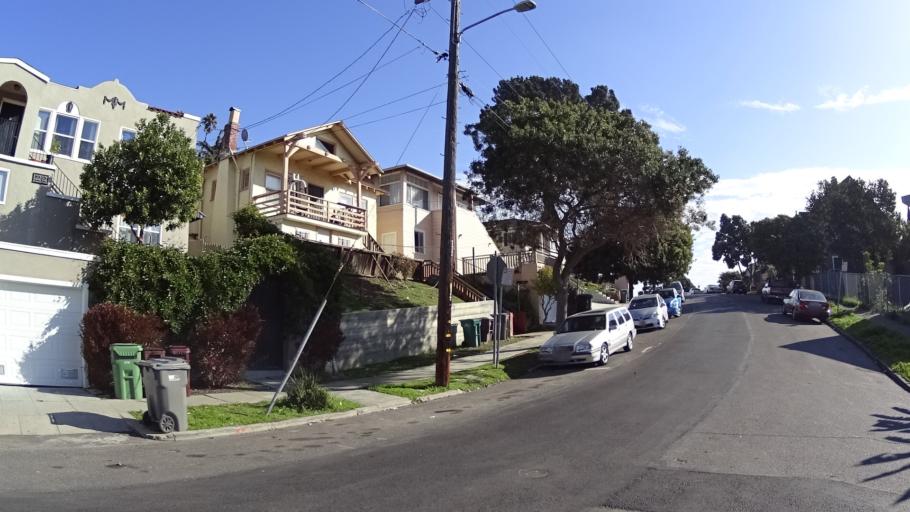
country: US
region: California
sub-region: Alameda County
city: Alameda
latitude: 37.7925
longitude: -122.2300
